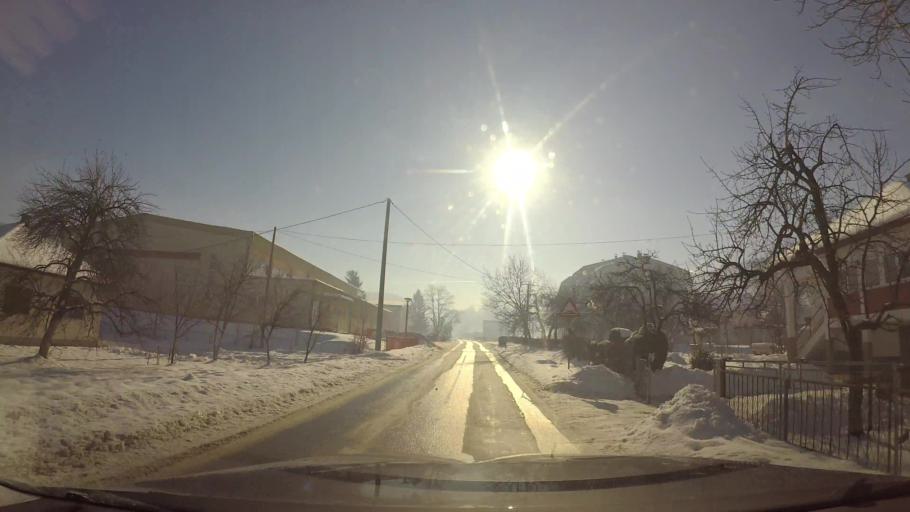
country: BA
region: Federation of Bosnia and Herzegovina
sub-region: Kanton Sarajevo
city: Sarajevo
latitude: 43.7943
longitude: 18.3527
